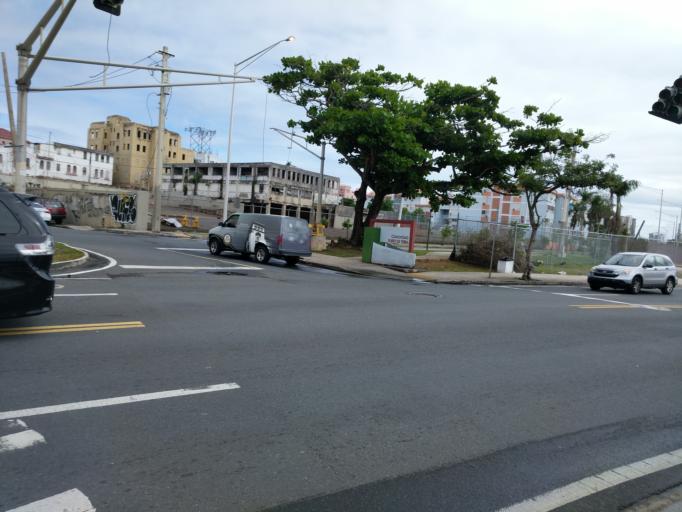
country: PR
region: San Juan
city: San Juan
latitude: 18.4643
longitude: -66.1035
